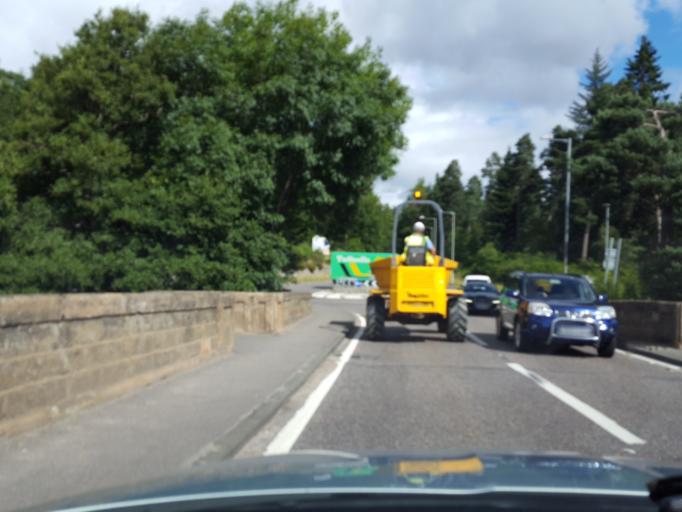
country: GB
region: Scotland
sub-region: Highland
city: Grantown on Spey
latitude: 57.3217
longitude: -3.6061
